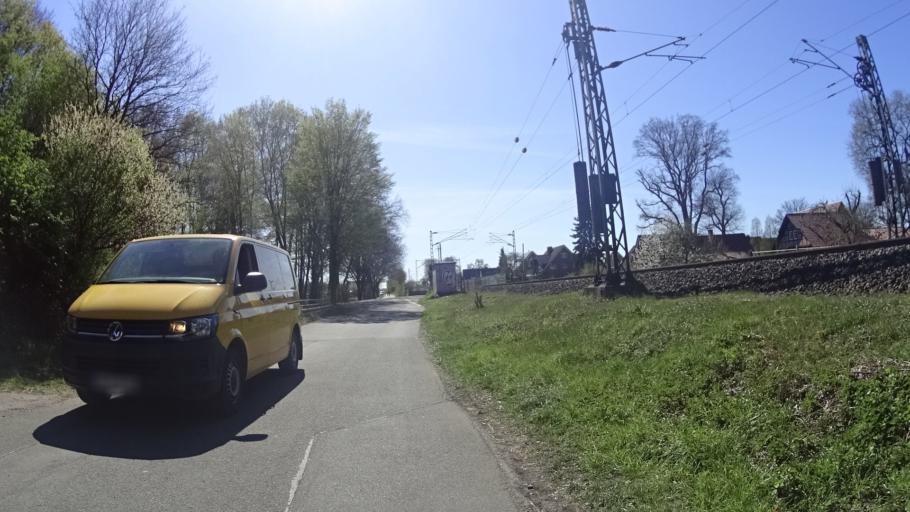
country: DE
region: North Rhine-Westphalia
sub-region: Regierungsbezirk Munster
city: Haltern
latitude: 51.7761
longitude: 7.2319
